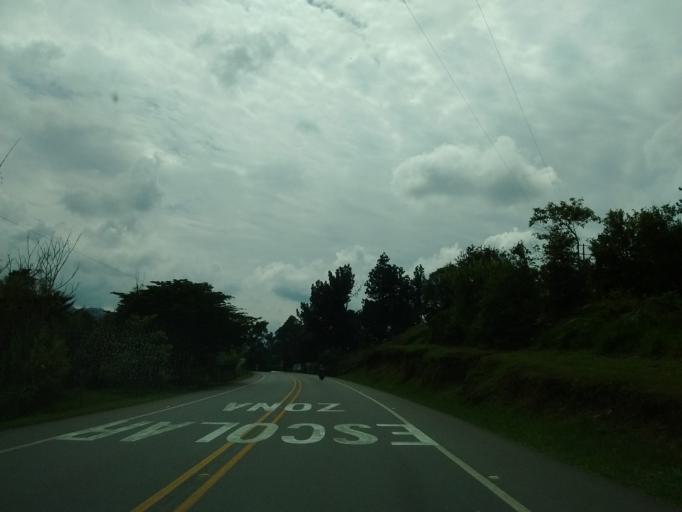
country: CO
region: Cauca
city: Cajibio
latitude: 2.7053
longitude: -76.5390
